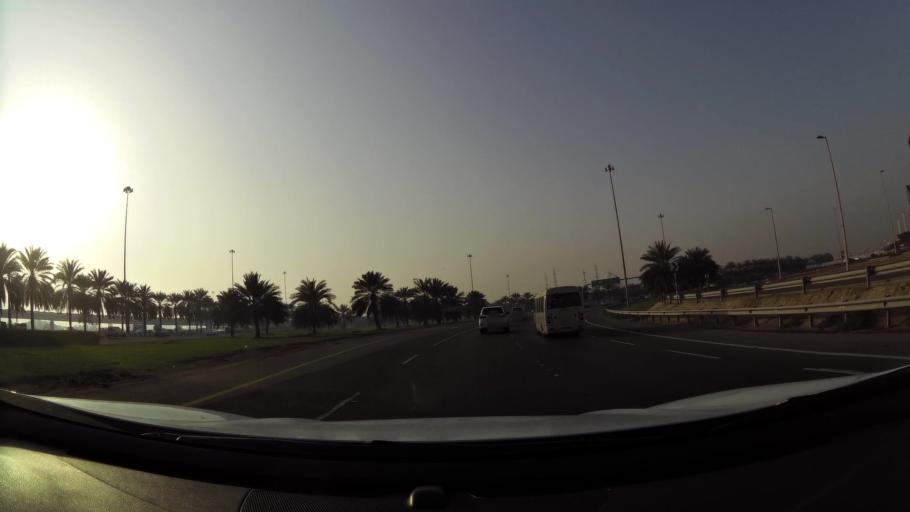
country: AE
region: Abu Dhabi
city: Abu Dhabi
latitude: 24.4240
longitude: 54.4754
